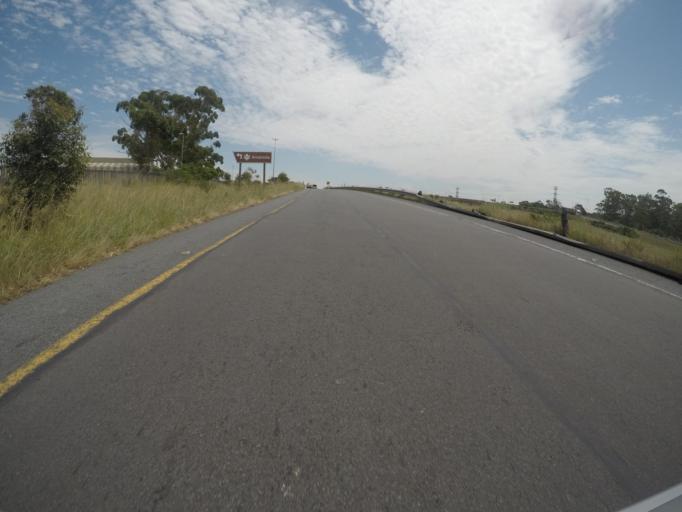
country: ZA
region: Eastern Cape
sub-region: Buffalo City Metropolitan Municipality
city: East London
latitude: -32.9710
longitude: 27.8522
